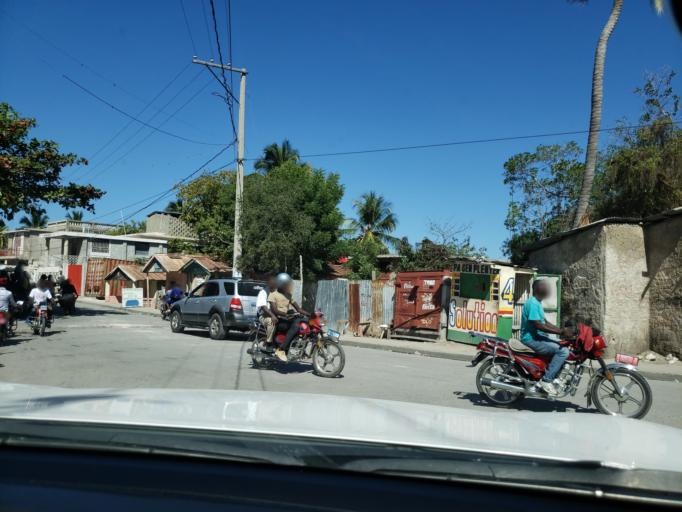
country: HT
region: Nippes
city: Miragoane
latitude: 18.4427
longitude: -73.0923
